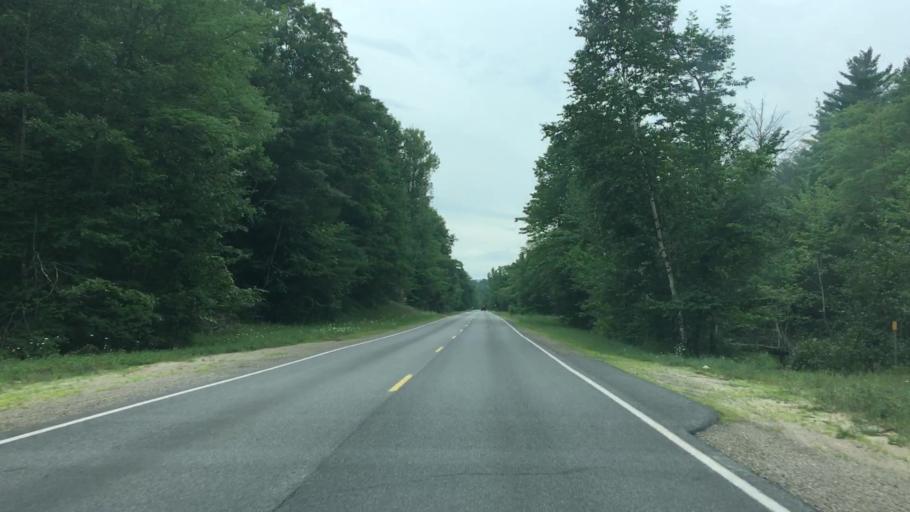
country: US
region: New York
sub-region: Clinton County
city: Peru
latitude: 44.4858
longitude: -73.5956
